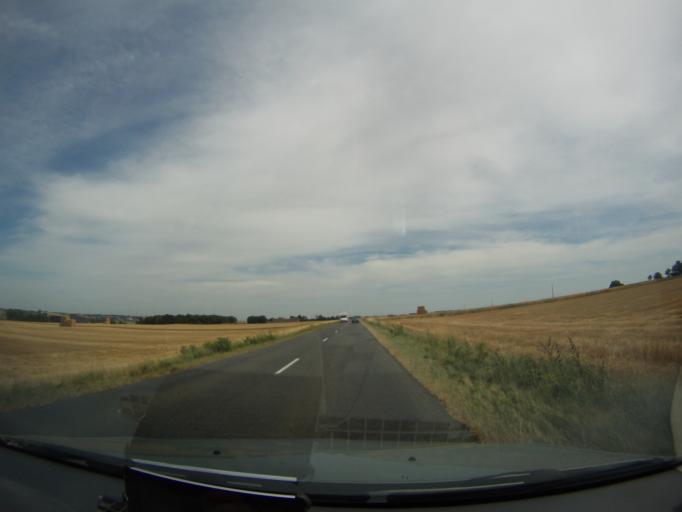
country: FR
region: Poitou-Charentes
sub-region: Departement de la Vienne
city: Saint-Jean-de-Sauves
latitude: 46.7914
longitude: 0.1170
